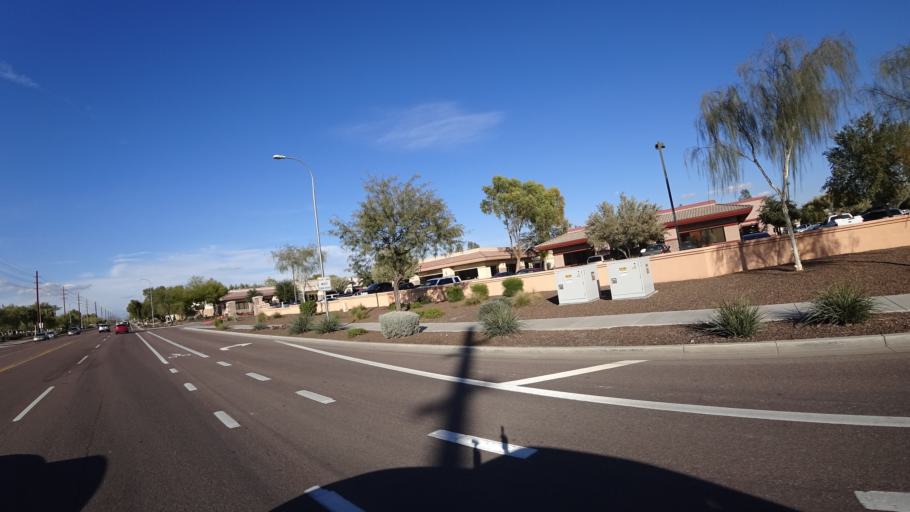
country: US
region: Arizona
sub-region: Maricopa County
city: Peoria
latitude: 33.6124
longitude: -112.2375
